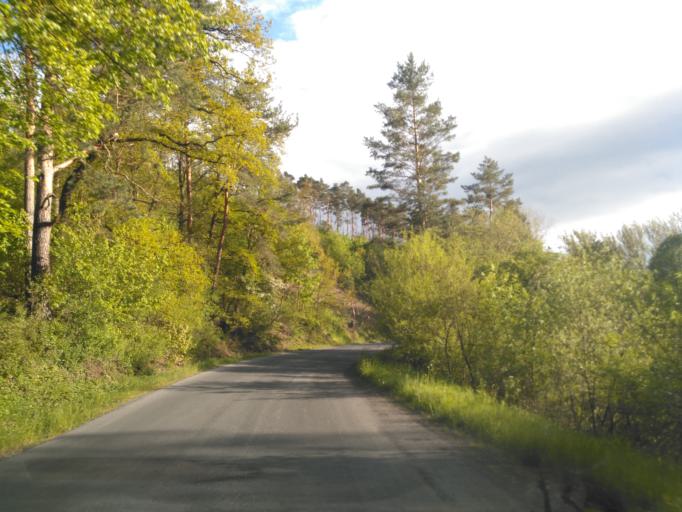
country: CZ
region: Central Bohemia
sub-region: Okres Beroun
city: Kraluv Dvur
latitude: 49.9272
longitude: 14.0483
